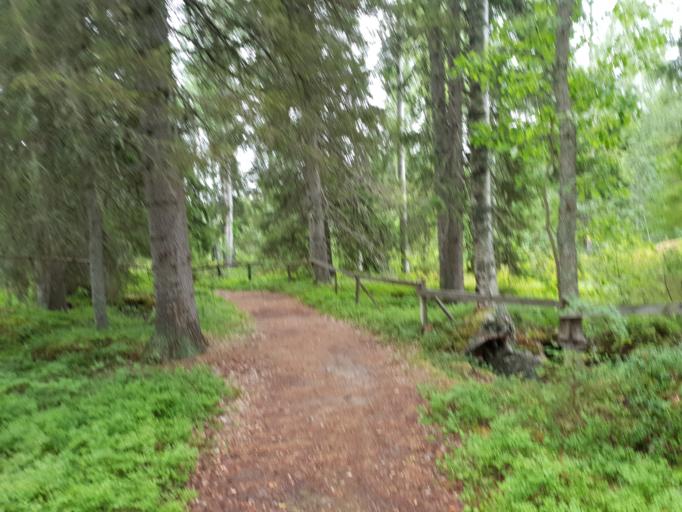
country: SE
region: Vaesterbotten
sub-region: Skelleftea Kommun
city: Viken
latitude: 64.8004
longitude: 20.7381
